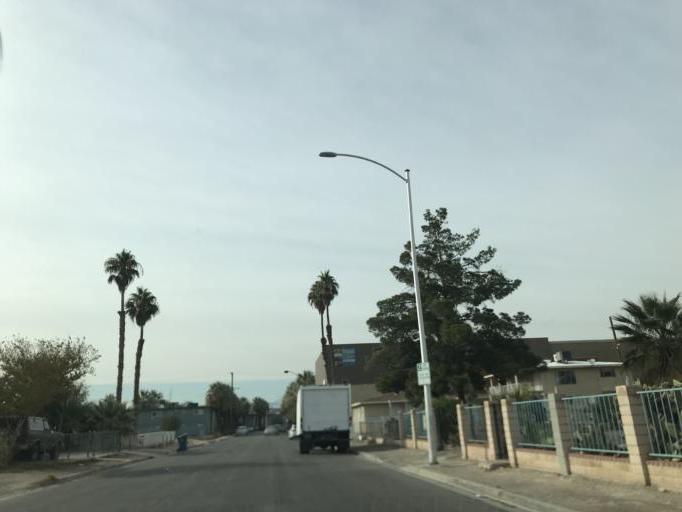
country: US
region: Nevada
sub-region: Clark County
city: Las Vegas
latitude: 36.1465
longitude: -115.1590
